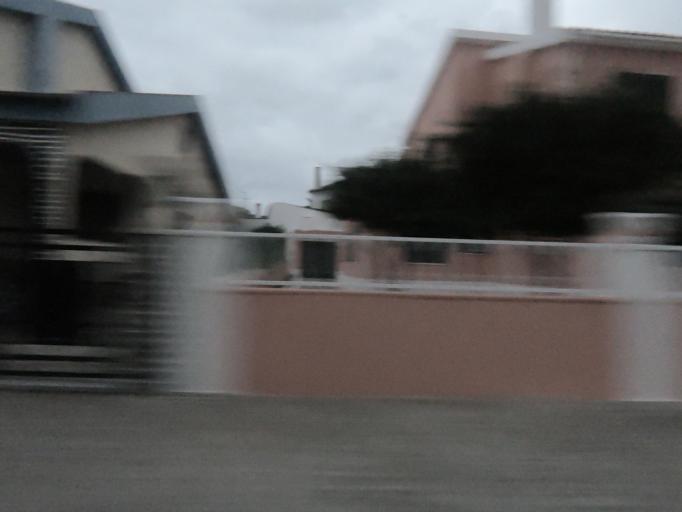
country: PT
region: Setubal
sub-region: Seixal
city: Amora
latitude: 38.6017
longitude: -9.1387
